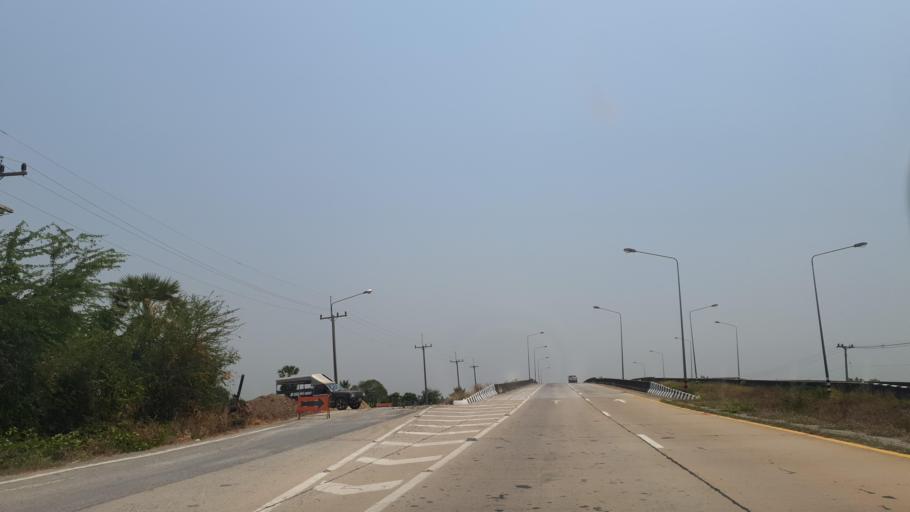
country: TH
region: Suphan Buri
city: Suphan Buri
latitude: 14.5483
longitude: 100.0814
